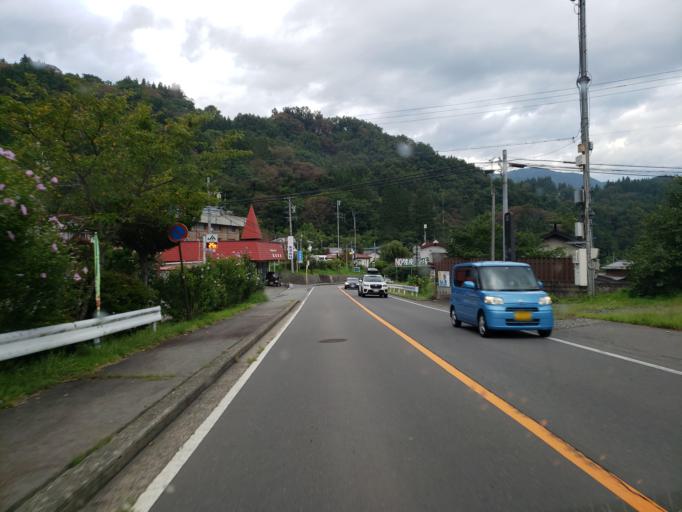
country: JP
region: Nagano
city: Nagano-shi
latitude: 36.6111
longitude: 138.0364
